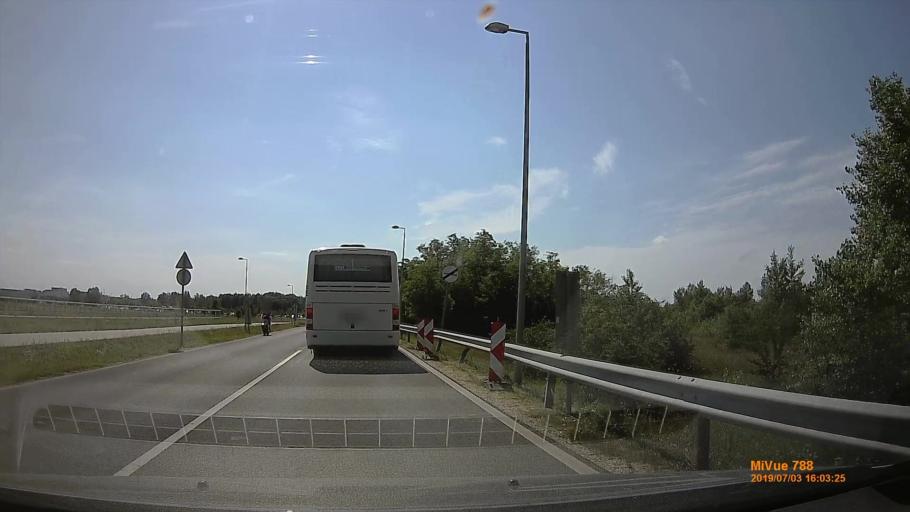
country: HU
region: Gyor-Moson-Sopron
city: Gyor
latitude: 47.7058
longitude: 17.6940
